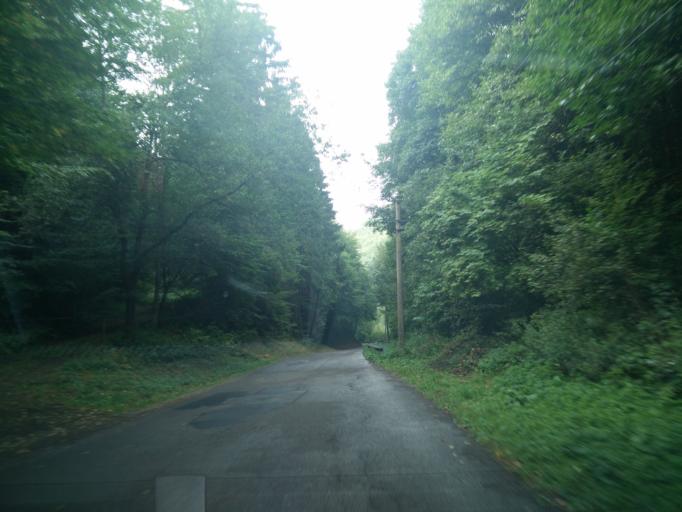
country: SK
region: Banskobystricky
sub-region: Okres Banska Bystrica
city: Banska Stiavnica
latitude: 48.4952
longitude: 18.8339
